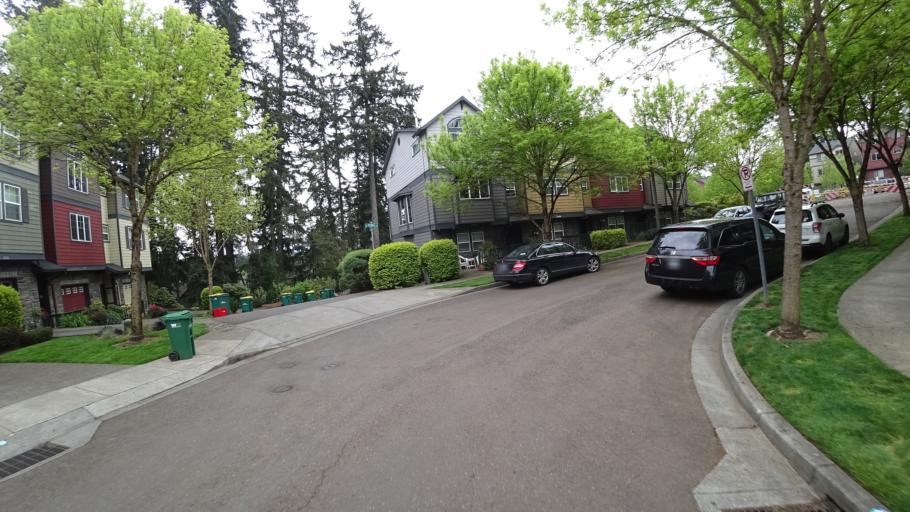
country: US
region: Oregon
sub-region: Washington County
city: Beaverton
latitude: 45.4509
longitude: -122.8357
